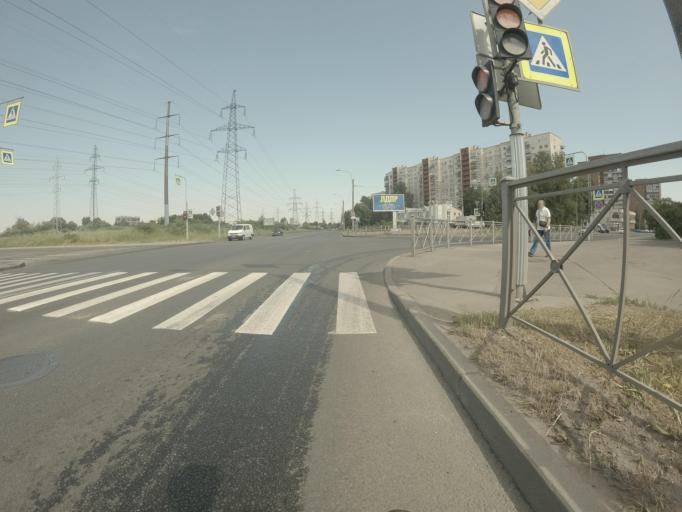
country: RU
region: St.-Petersburg
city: Krasnogvargeisky
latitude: 59.9484
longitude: 30.4610
